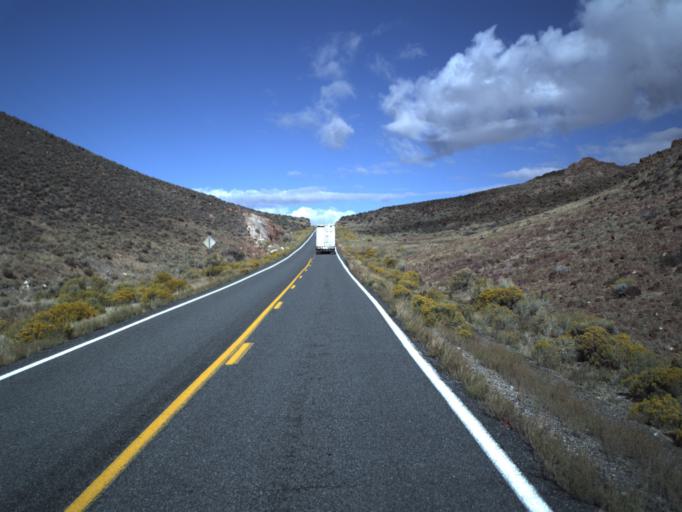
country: US
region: Utah
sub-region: Beaver County
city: Milford
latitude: 38.6127
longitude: -113.8380
